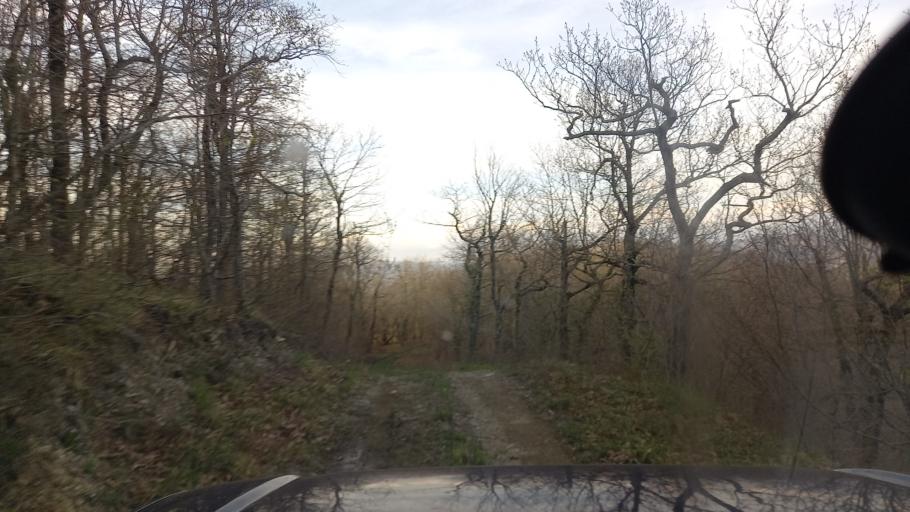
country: RU
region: Krasnodarskiy
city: Arkhipo-Osipovka
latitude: 44.3577
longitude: 38.5524
